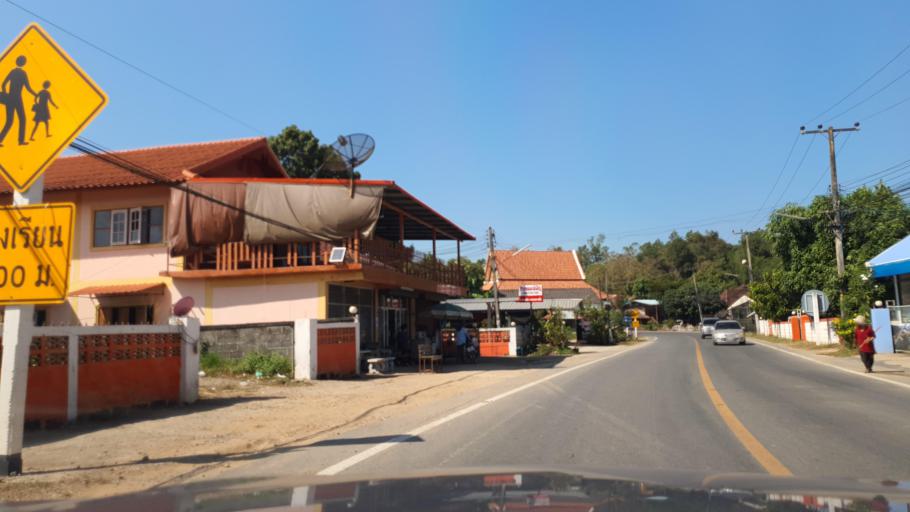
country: TH
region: Nan
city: Tha Wang Pha
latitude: 19.0817
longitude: 100.8808
